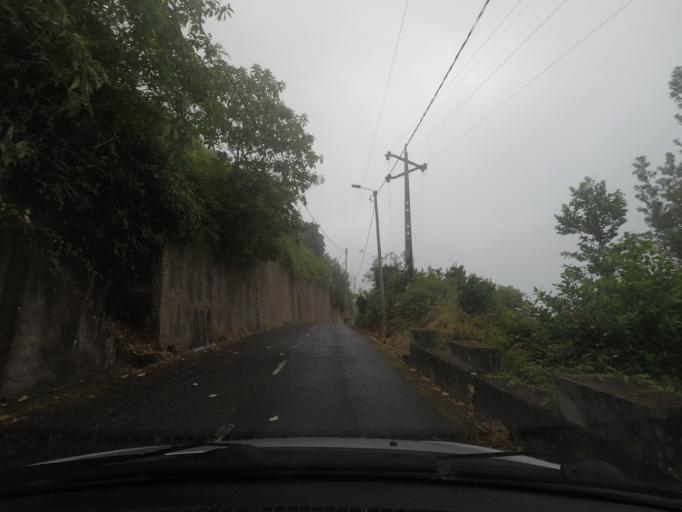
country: PT
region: Madeira
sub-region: Santana
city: Santana
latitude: 32.7771
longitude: -16.8669
